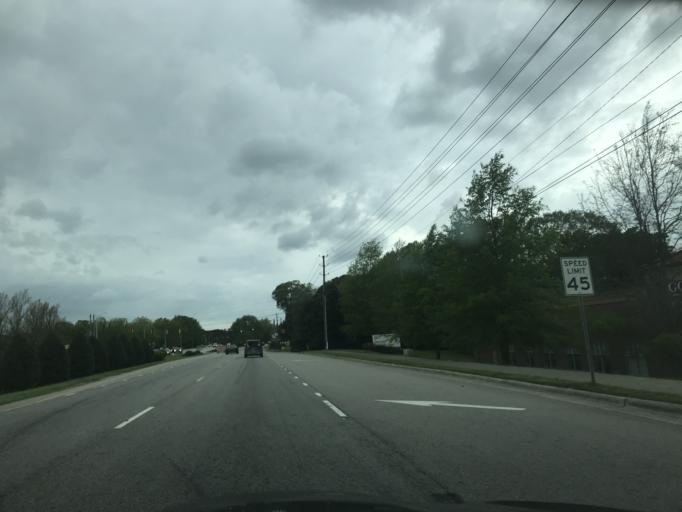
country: US
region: North Carolina
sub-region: Wake County
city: Knightdale
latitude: 35.7984
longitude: -78.4903
